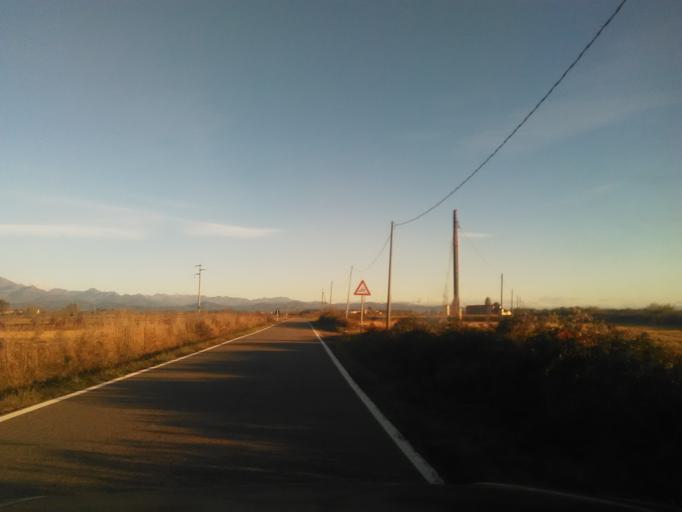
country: IT
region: Piedmont
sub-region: Provincia di Vercelli
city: Buronzo
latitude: 45.4906
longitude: 8.2807
